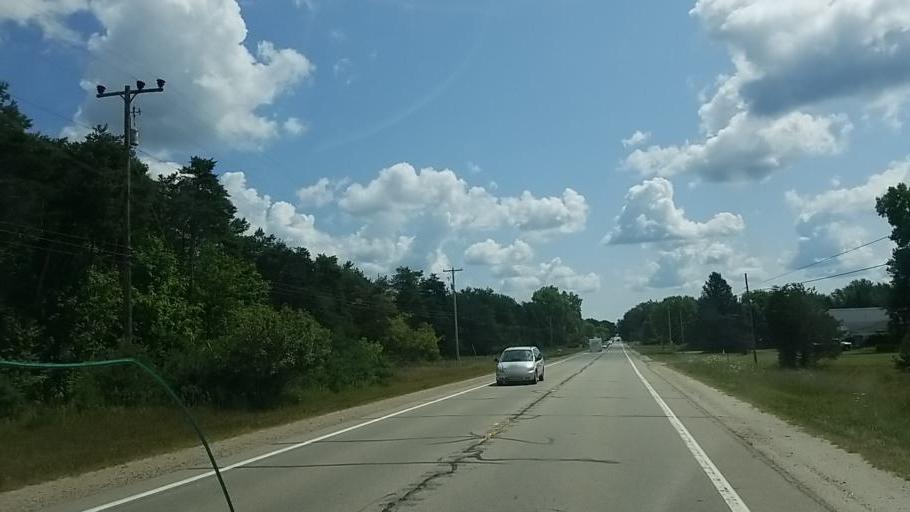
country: US
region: Michigan
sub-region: Muskegon County
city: Ravenna
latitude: 43.2352
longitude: -85.9669
